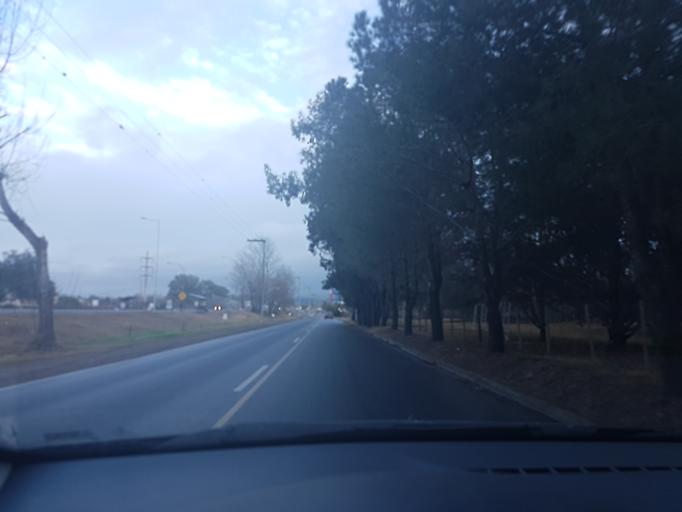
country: AR
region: Cordoba
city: Villa Allende
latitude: -31.3007
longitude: -64.2728
